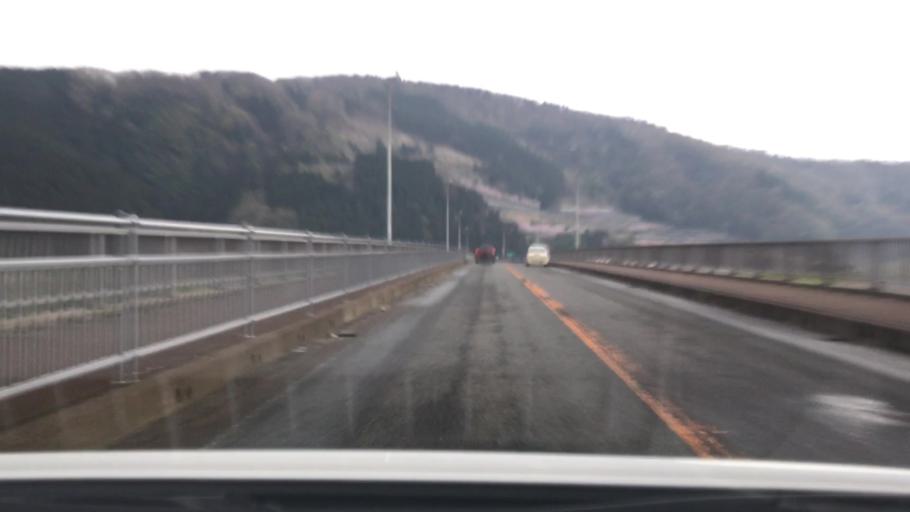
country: JP
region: Fukui
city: Fukui-shi
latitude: 36.0875
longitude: 136.1865
